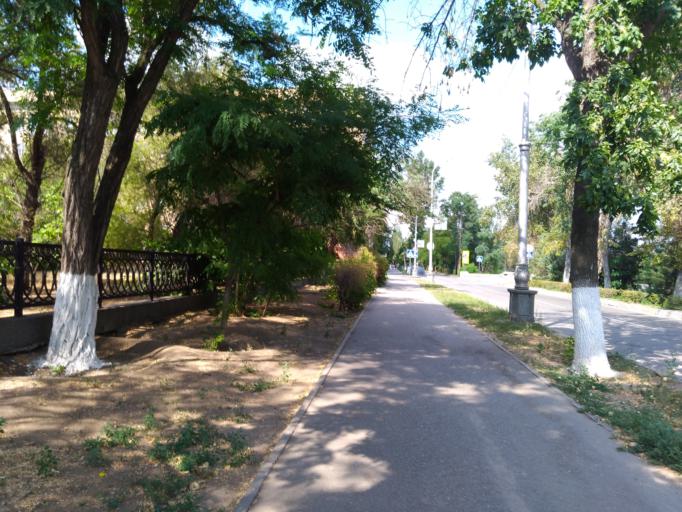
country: RU
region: Volgograd
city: Volgograd
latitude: 48.7093
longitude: 44.5280
